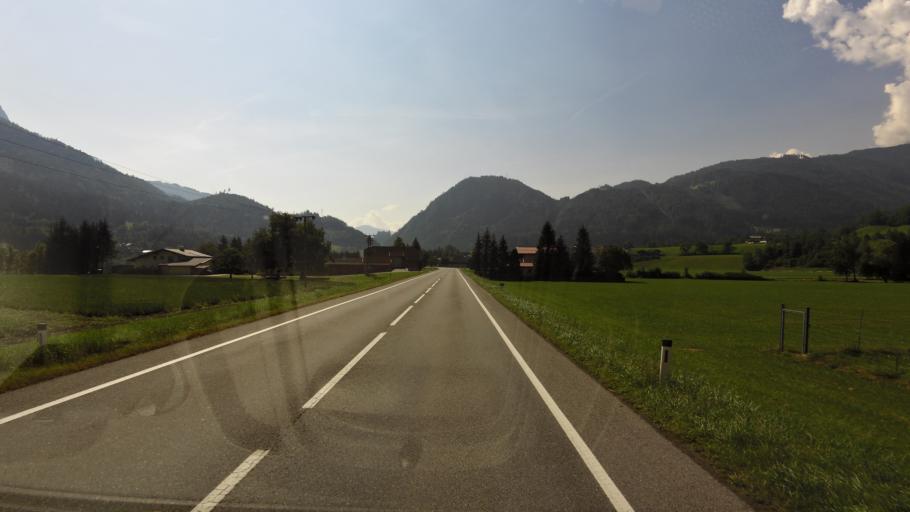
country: AT
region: Salzburg
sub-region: Politischer Bezirk Sankt Johann im Pongau
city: Werfen
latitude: 47.5011
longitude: 13.1705
